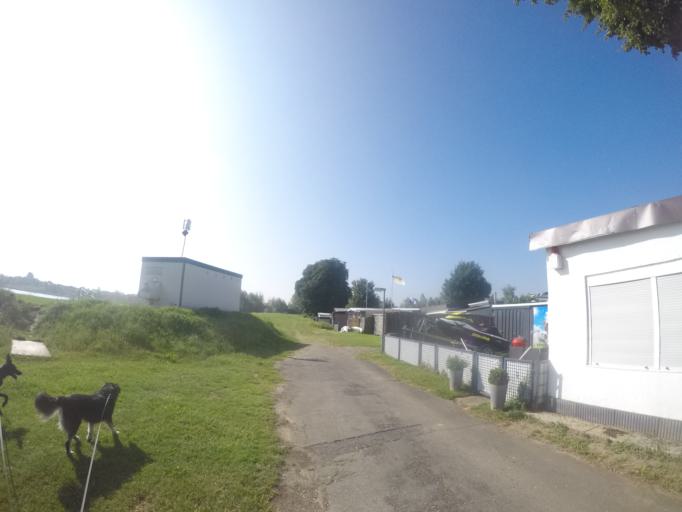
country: NL
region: Gelderland
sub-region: Gemeente Rheden
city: Rheden
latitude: 51.9943
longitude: 6.0378
